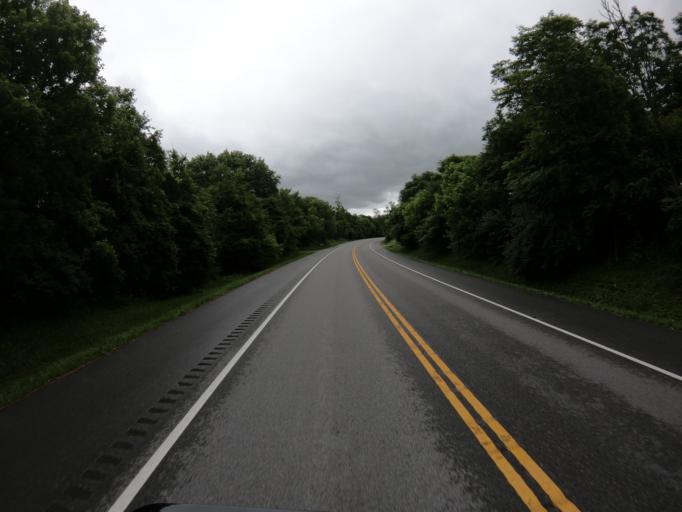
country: US
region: Maryland
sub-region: Washington County
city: Keedysville
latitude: 39.4909
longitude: -77.7002
